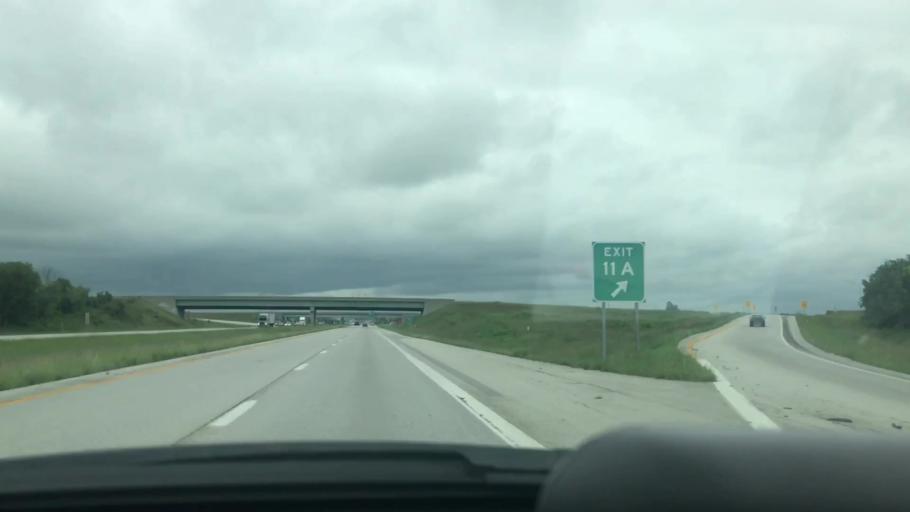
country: US
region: Missouri
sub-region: Jasper County
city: Duenweg
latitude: 37.0594
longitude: -94.4327
